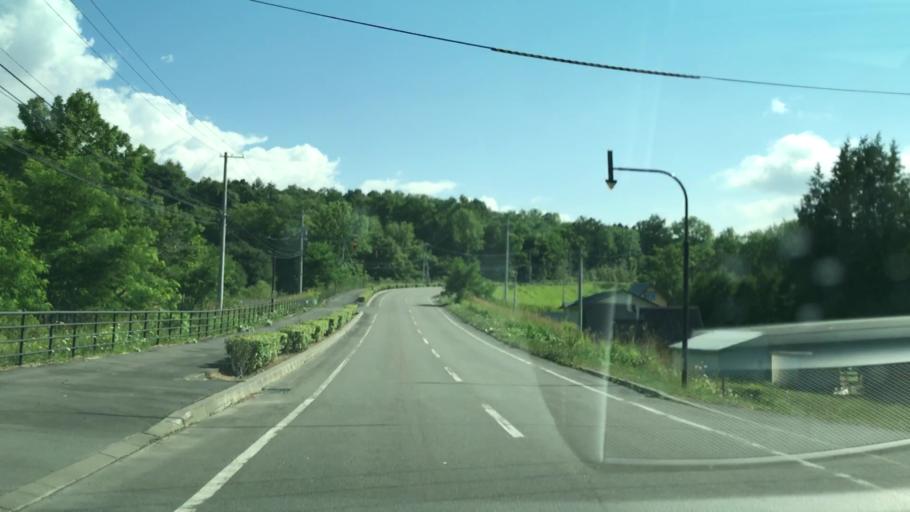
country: JP
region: Hokkaido
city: Shimo-furano
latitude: 42.8701
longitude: 142.4424
